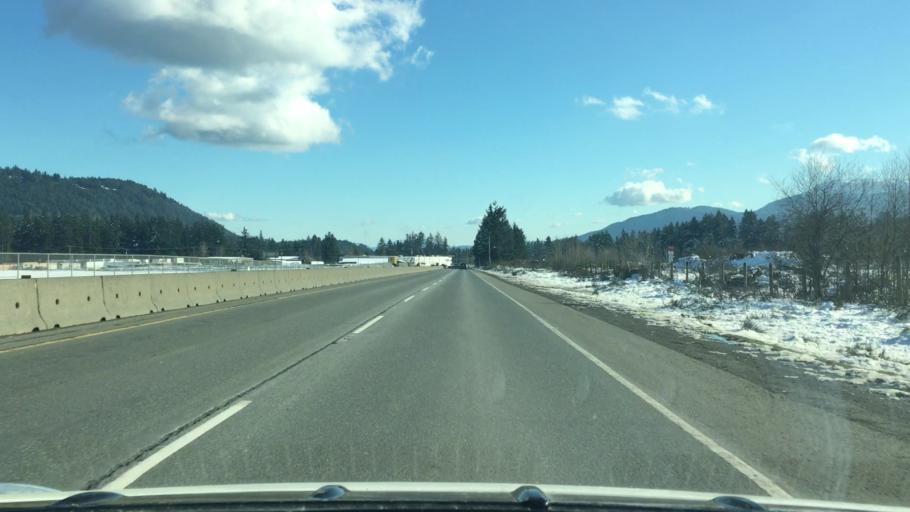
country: CA
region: British Columbia
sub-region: Cowichan Valley Regional District
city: Ladysmith
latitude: 49.0430
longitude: -123.8707
